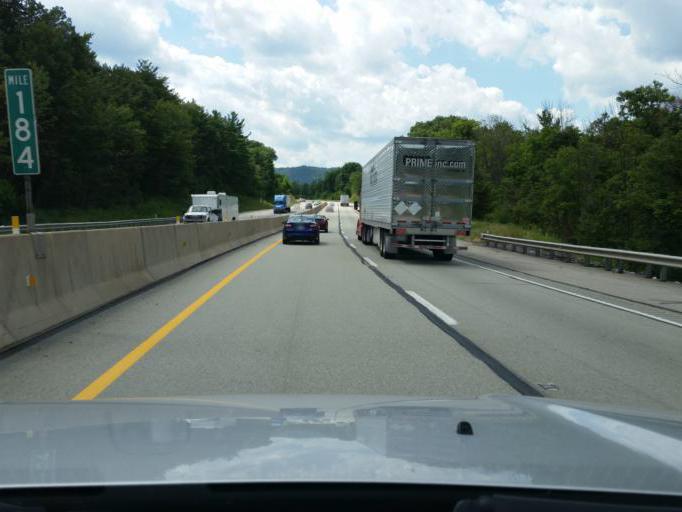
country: US
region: Pennsylvania
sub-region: Fulton County
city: McConnellsburg
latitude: 40.0758
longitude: -77.8875
